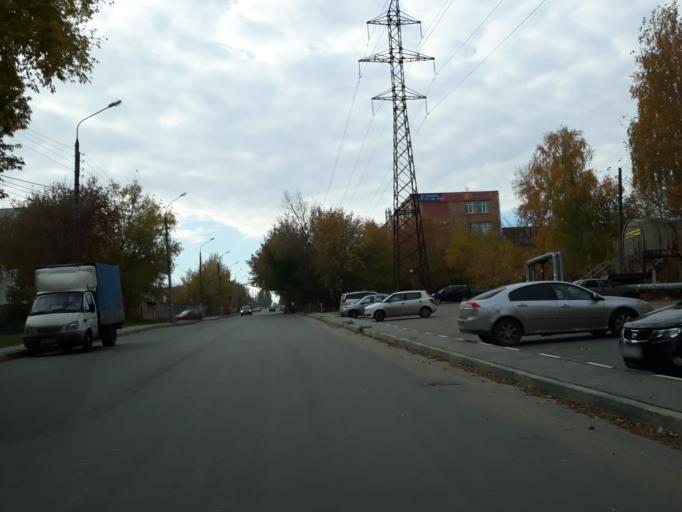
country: RU
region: Nizjnij Novgorod
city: Nizhniy Novgorod
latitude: 56.2470
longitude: 43.9822
